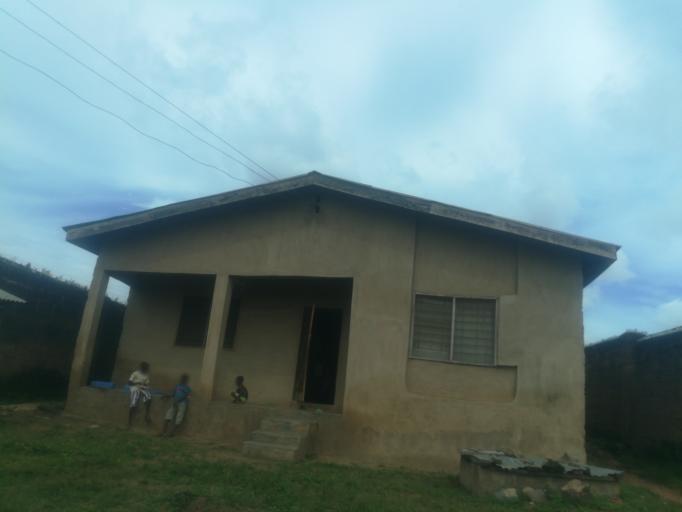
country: NG
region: Oyo
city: Ibadan
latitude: 7.3657
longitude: 3.9718
